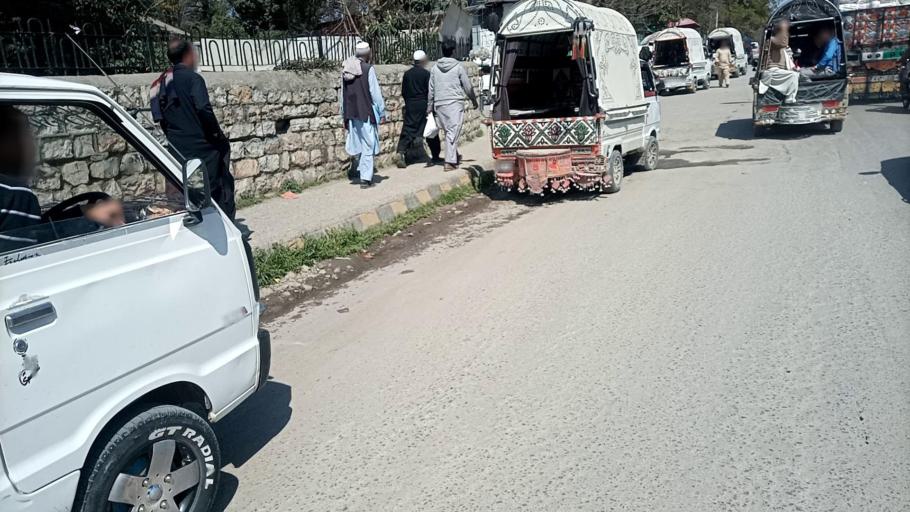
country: PK
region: Khyber Pakhtunkhwa
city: Abbottabad
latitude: 34.1483
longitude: 73.2161
